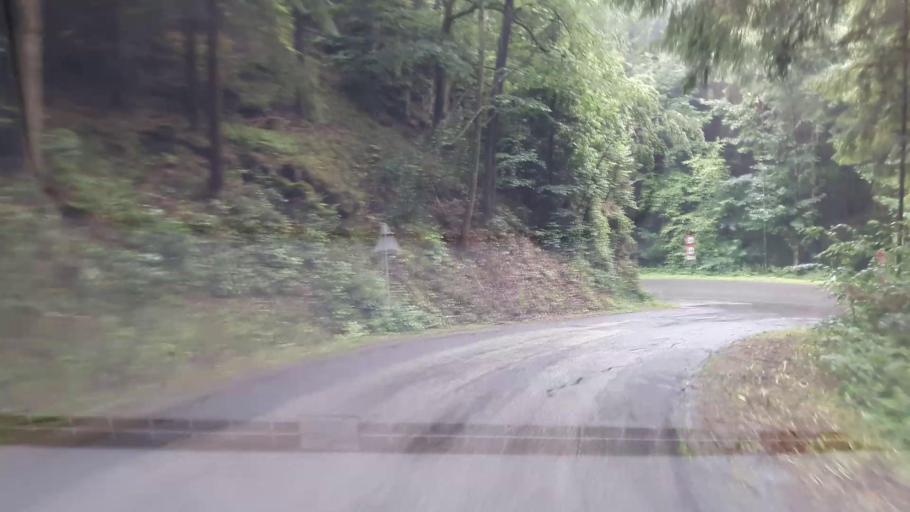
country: AT
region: Lower Austria
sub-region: Politischer Bezirk Krems
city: Aggsbach
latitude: 48.2873
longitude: 15.3794
